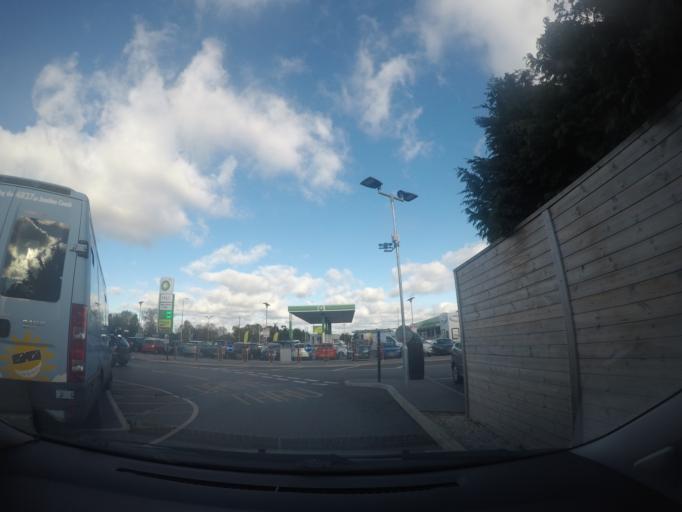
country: GB
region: England
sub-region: City of York
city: Nether Poppleton
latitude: 53.9716
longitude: -1.1433
